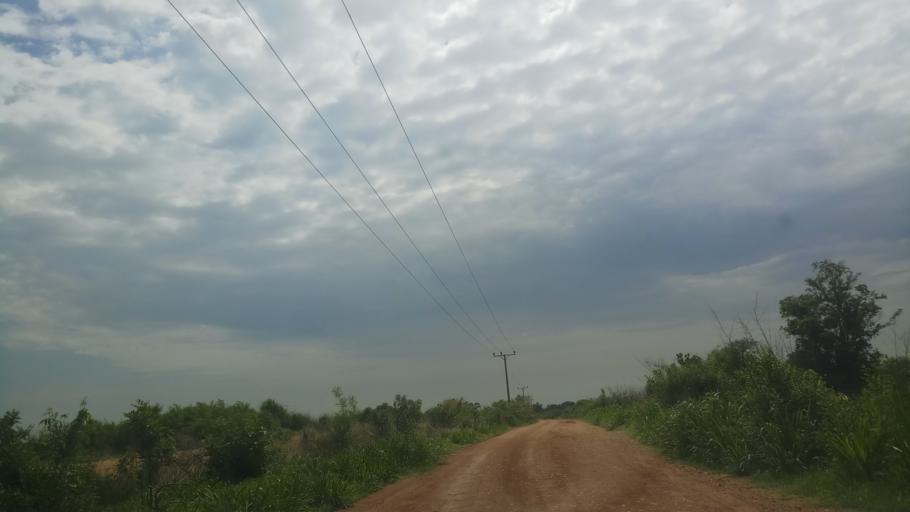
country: ET
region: Gambela
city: Gambela
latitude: 8.2159
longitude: 34.5511
